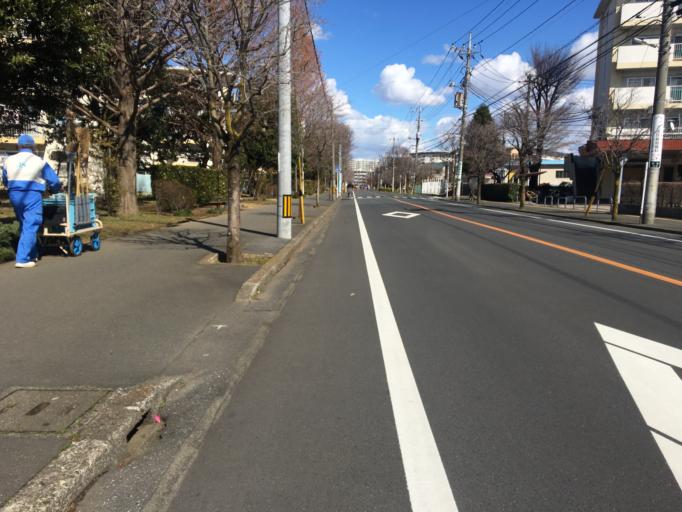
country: JP
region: Saitama
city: Shiki
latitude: 35.8219
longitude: 139.5564
